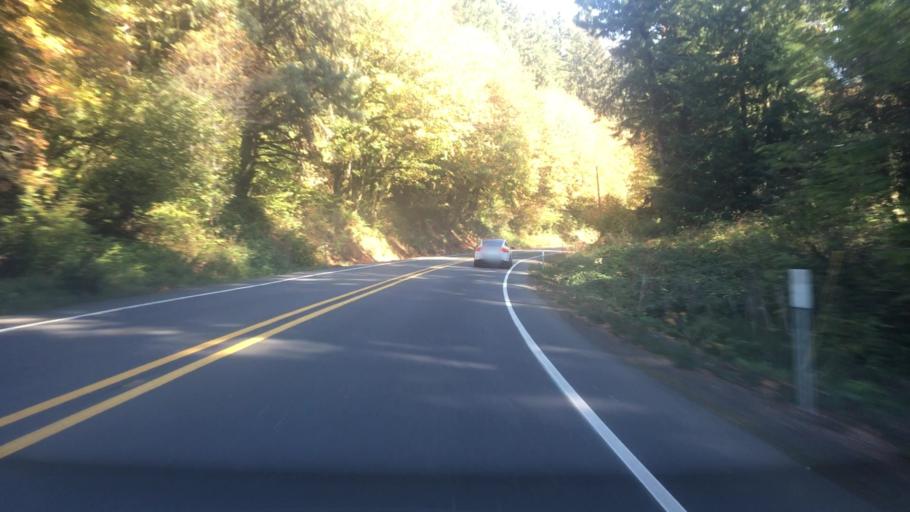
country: US
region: Oregon
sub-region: Lincoln County
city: Rose Lodge
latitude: 45.0259
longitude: -123.8242
